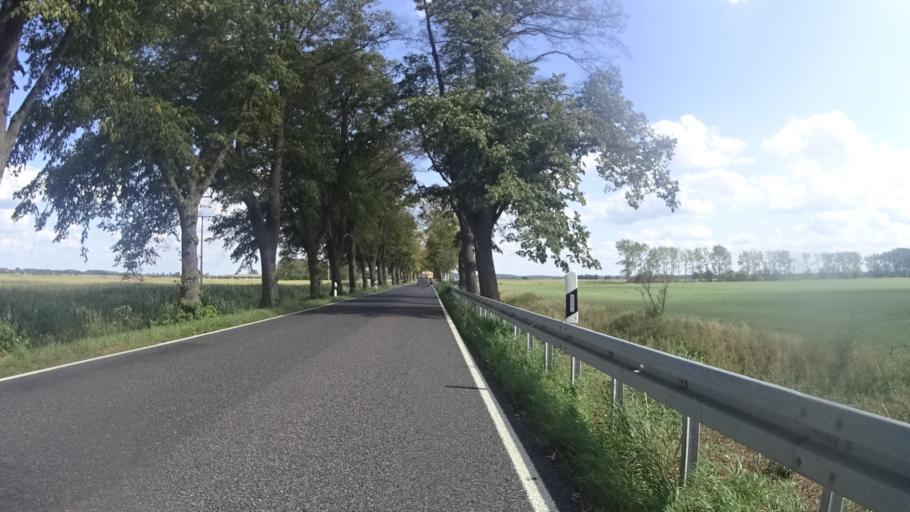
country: DE
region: Brandenburg
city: Rhinow
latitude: 52.7674
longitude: 12.2764
